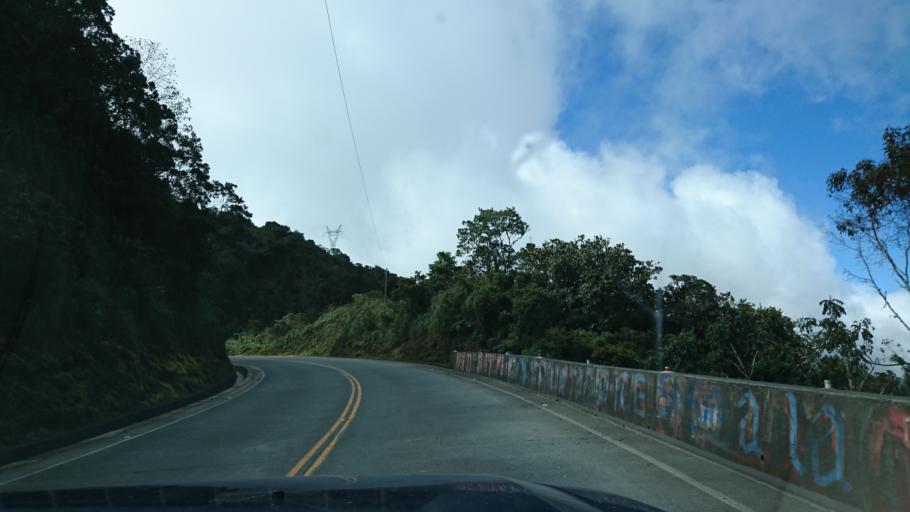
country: BO
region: La Paz
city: Coroico
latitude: -16.2867
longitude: -67.8461
